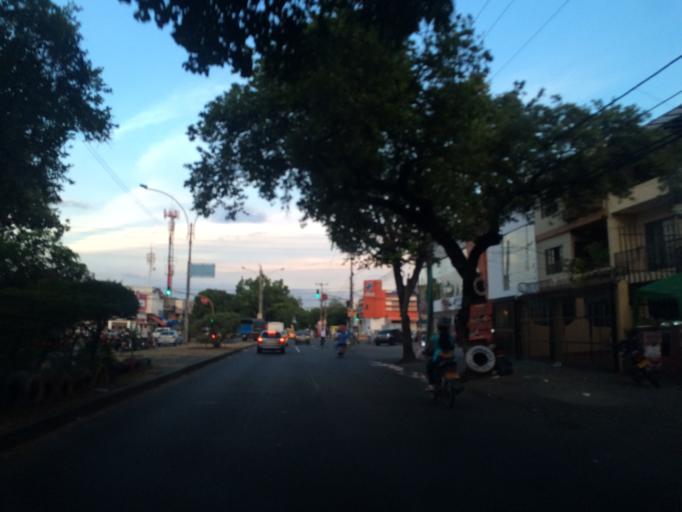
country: CO
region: Valle del Cauca
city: Cali
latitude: 3.4146
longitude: -76.5334
